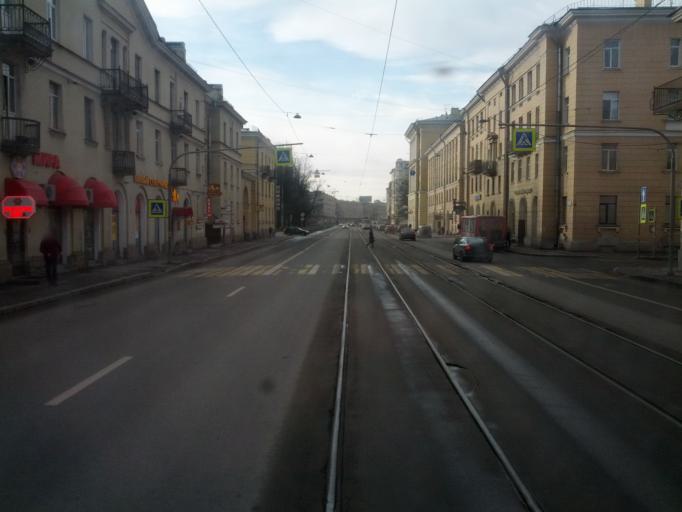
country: RU
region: Leningrad
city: Kalininskiy
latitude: 59.9498
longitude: 30.4146
